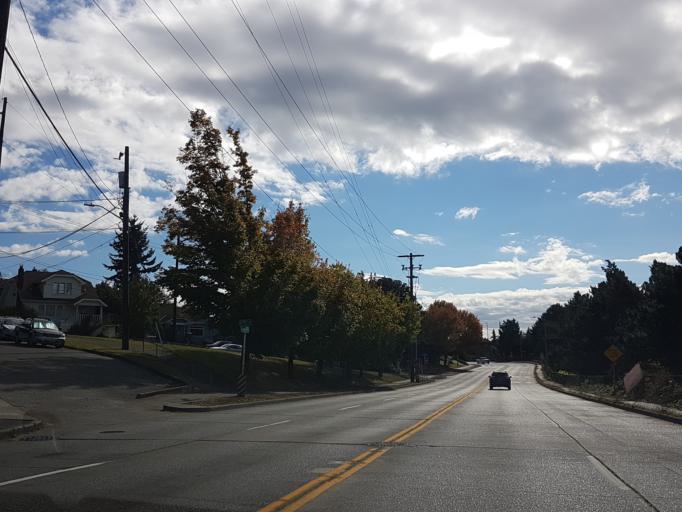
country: US
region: Washington
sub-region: King County
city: Shoreline
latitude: 47.6847
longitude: -122.3225
